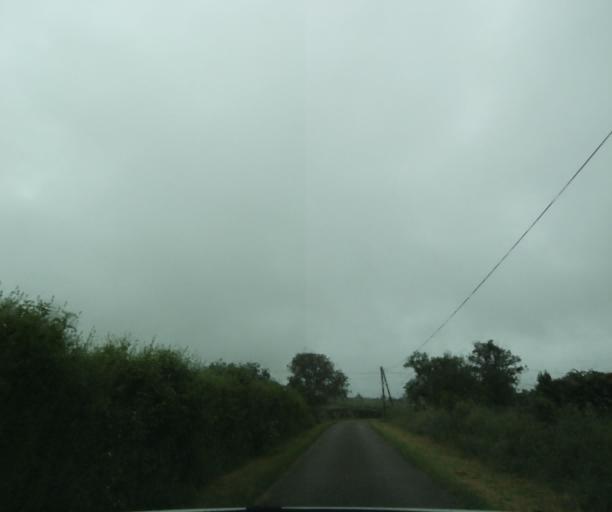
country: FR
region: Bourgogne
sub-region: Departement de Saone-et-Loire
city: Charolles
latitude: 46.4584
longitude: 4.2114
